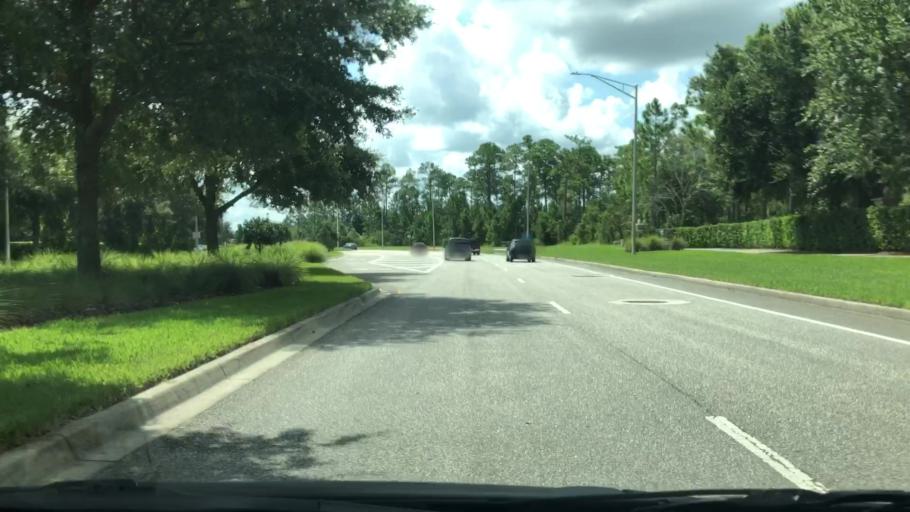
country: US
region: Florida
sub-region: Saint Johns County
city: Fruit Cove
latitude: 30.1316
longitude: -81.5436
